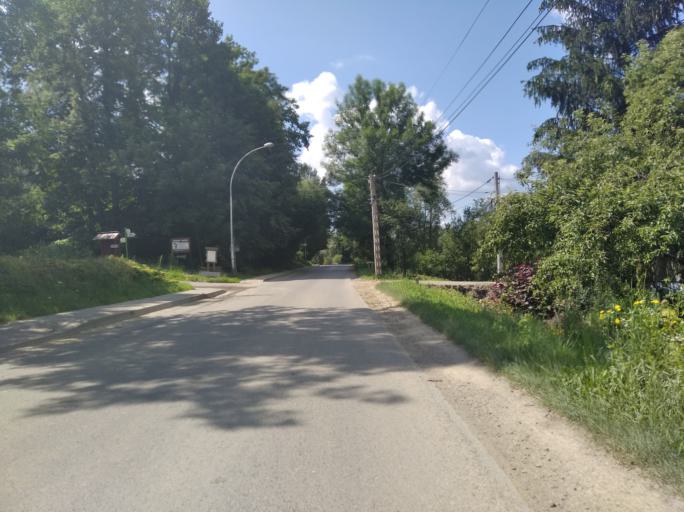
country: PL
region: Subcarpathian Voivodeship
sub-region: Powiat rzeszowski
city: Dynow
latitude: 49.8007
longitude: 22.2454
